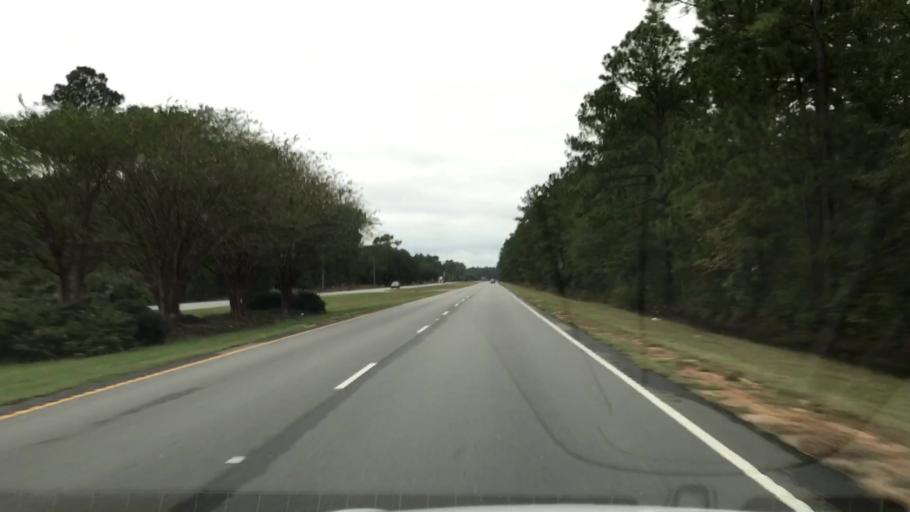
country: US
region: South Carolina
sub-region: Georgetown County
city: Georgetown
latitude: 33.2368
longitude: -79.3757
